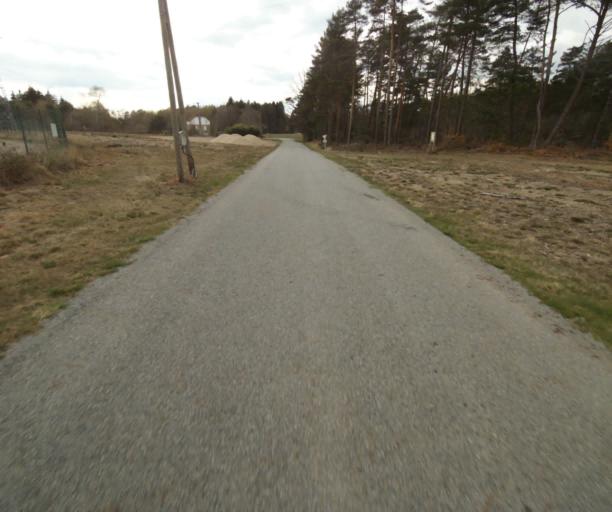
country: FR
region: Limousin
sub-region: Departement de la Correze
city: Saint-Privat
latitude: 45.2100
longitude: 2.0057
